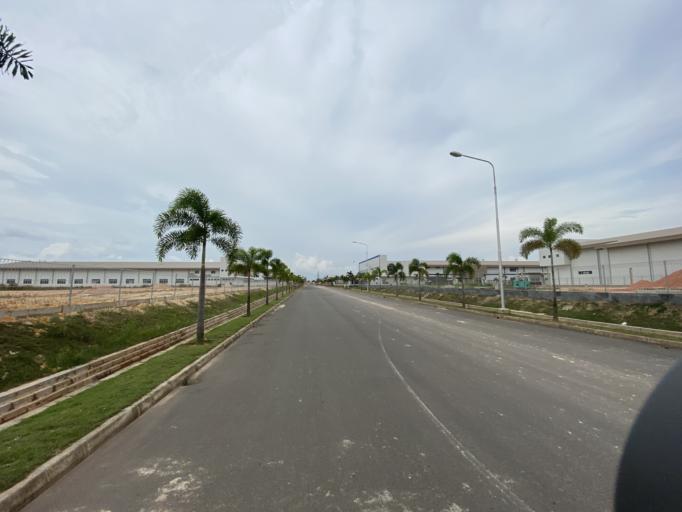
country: SG
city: Singapore
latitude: 1.0214
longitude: 103.9480
